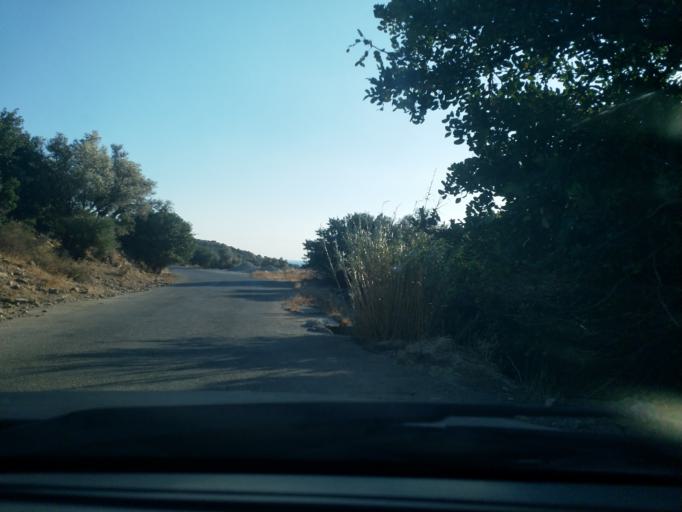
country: GR
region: Crete
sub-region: Nomos Rethymnis
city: Agia Galini
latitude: 35.1243
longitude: 24.5596
